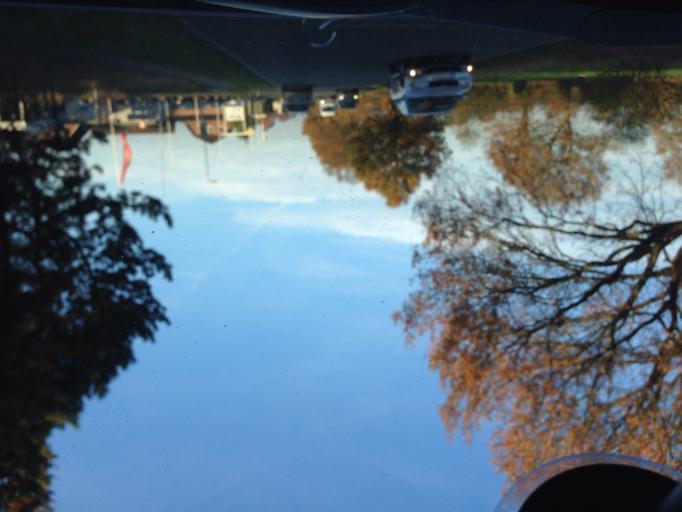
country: DE
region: Schleswig-Holstein
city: Stapelfeld
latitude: 53.6053
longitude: 10.2057
